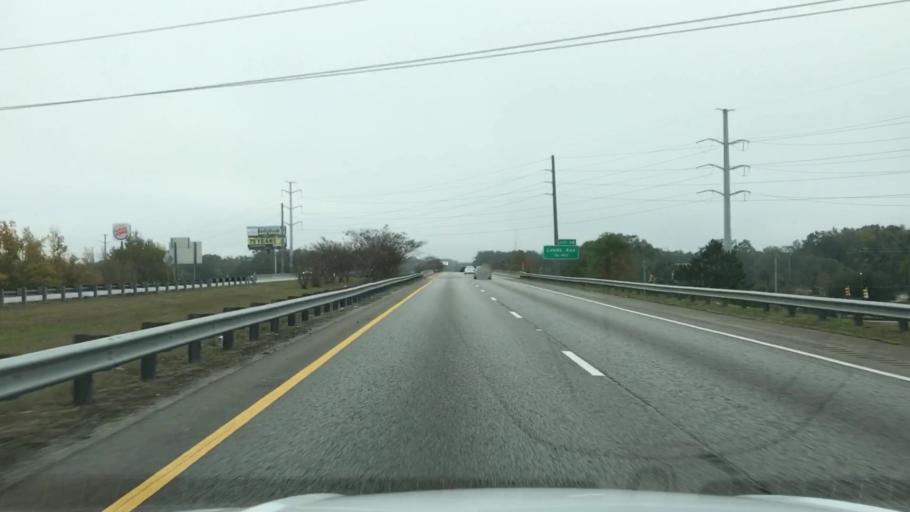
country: US
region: South Carolina
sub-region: Charleston County
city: North Charleston
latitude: 32.8557
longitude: -80.0221
